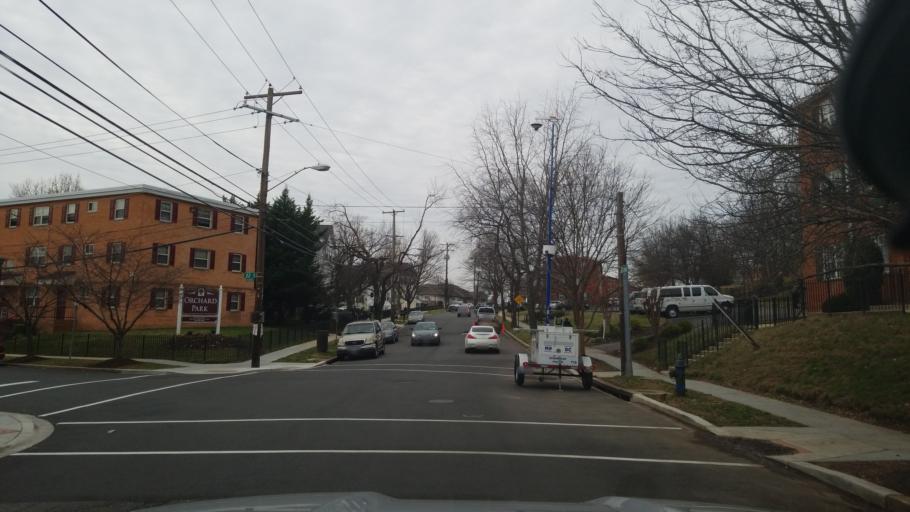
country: US
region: Maryland
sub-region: Prince George's County
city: Hillcrest Heights
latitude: 38.8475
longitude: -76.9728
